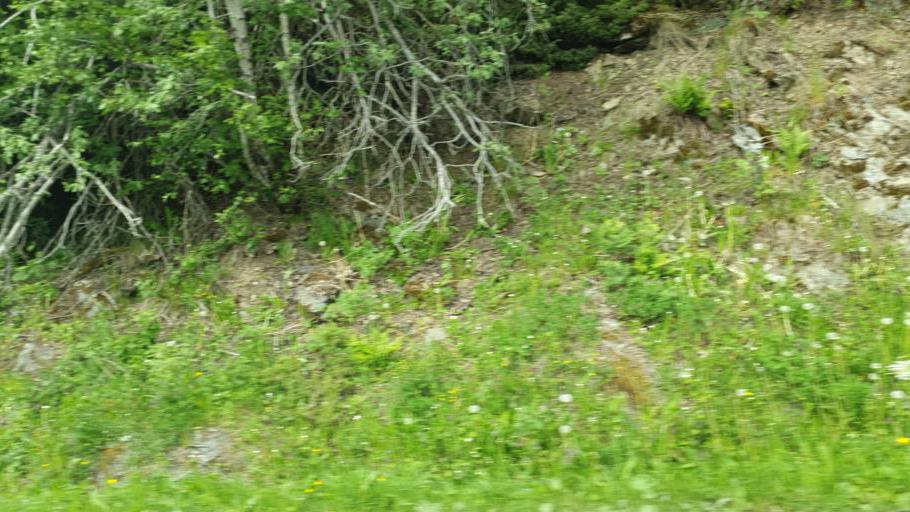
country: NO
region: Nord-Trondelag
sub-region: Leksvik
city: Leksvik
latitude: 63.6370
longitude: 10.5806
